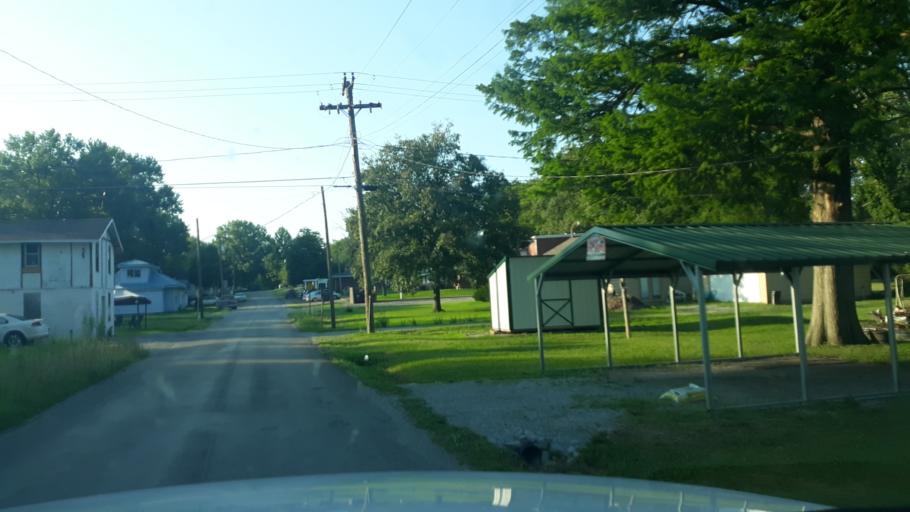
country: US
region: Illinois
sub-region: Saline County
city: Eldorado
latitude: 37.8110
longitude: -88.4319
